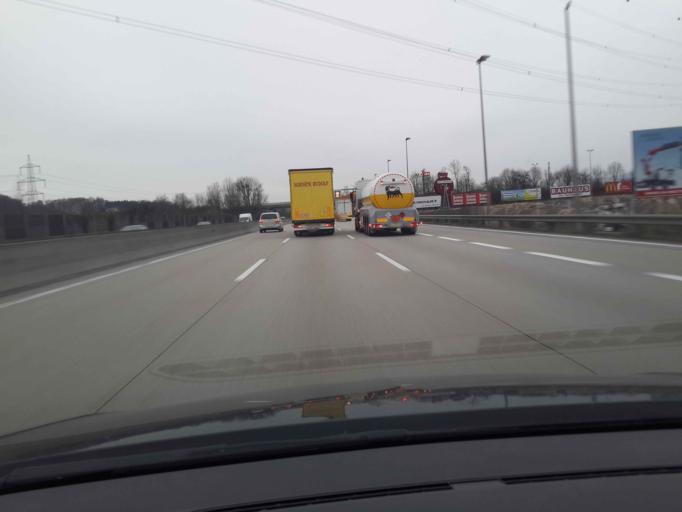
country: AT
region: Upper Austria
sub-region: Politischer Bezirk Linz-Land
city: Asten
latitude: 48.2206
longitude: 14.4010
